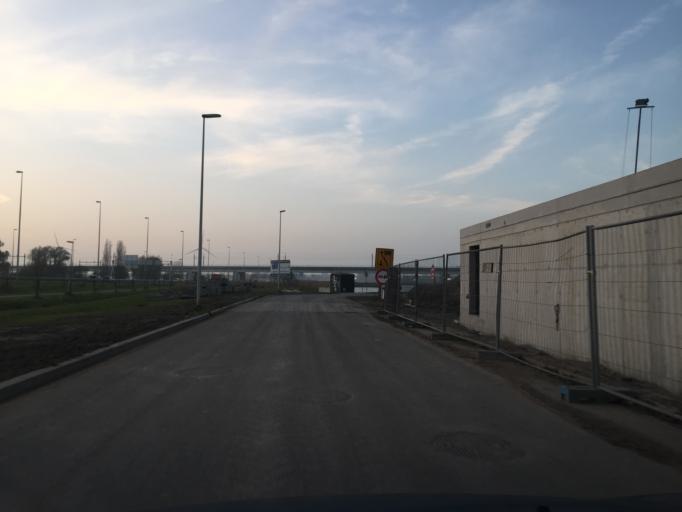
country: NL
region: South Holland
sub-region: Gemeente Lansingerland
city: Bleiswijk
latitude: 52.0383
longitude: 4.5343
